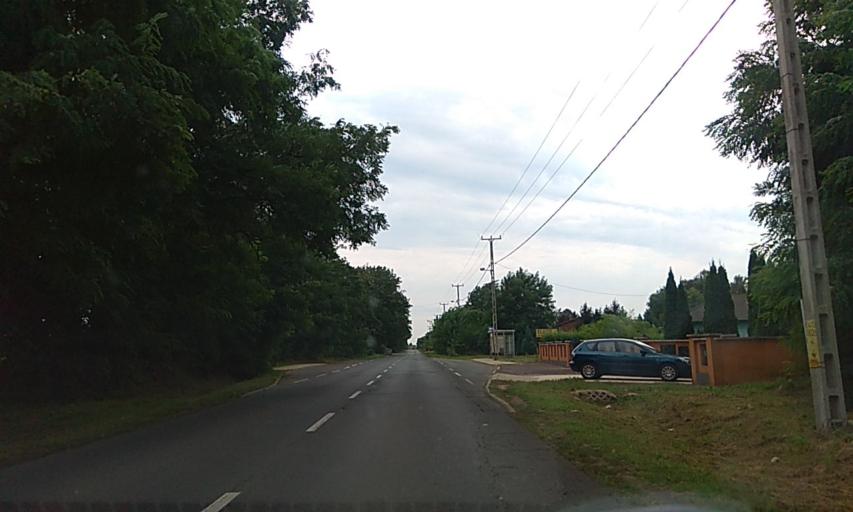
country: HU
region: Szabolcs-Szatmar-Bereg
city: Kotaj
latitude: 48.0229
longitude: 21.6814
